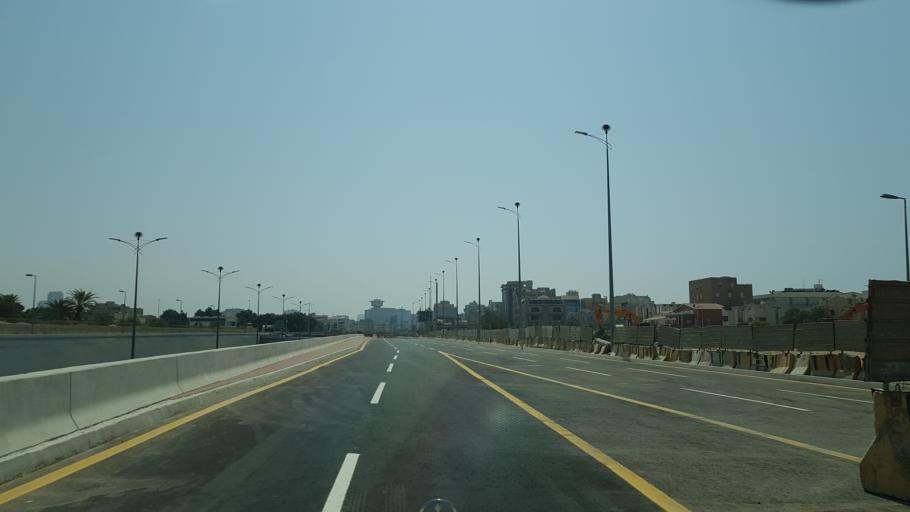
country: SA
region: Makkah
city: Jeddah
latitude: 21.5259
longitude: 39.1625
